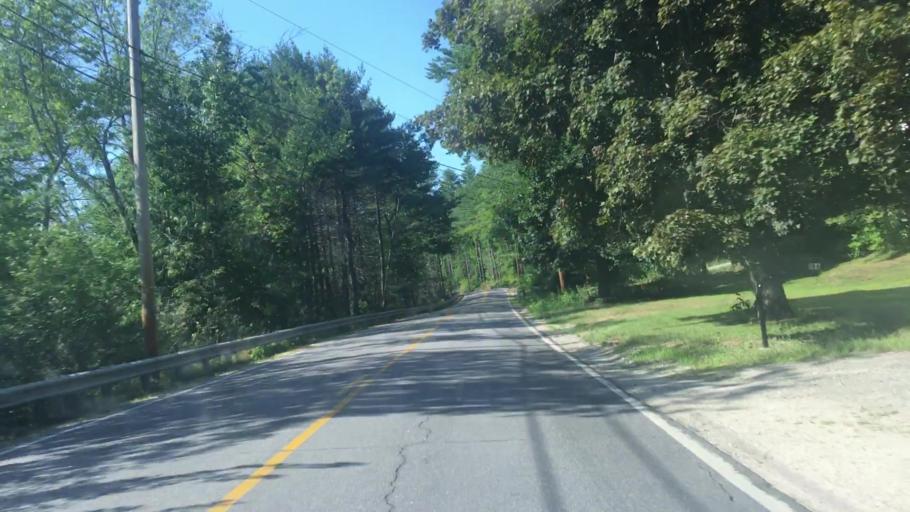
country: US
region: Maine
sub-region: York County
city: Hollis Center
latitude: 43.6546
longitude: -70.5962
